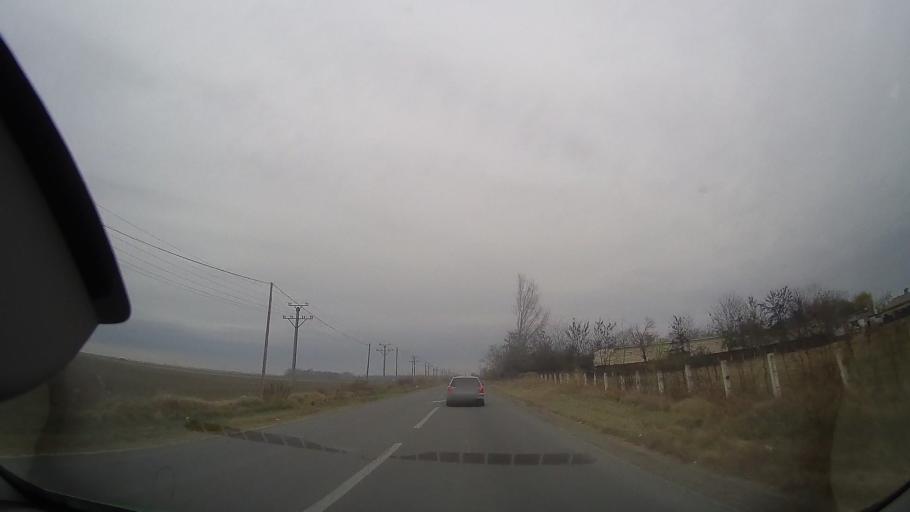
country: RO
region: Ialomita
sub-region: Oras Amara
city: Amara
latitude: 44.5861
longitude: 27.3332
